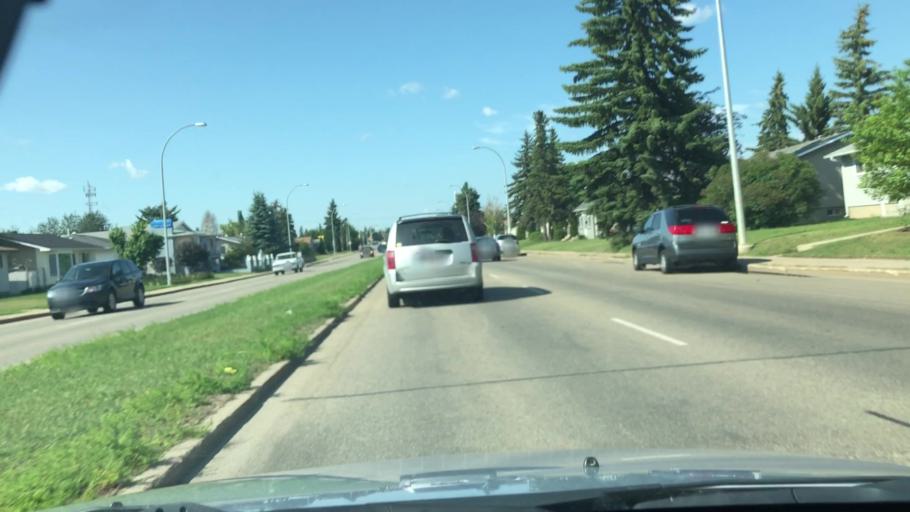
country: CA
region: Alberta
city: Edmonton
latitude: 53.5959
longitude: -113.4429
